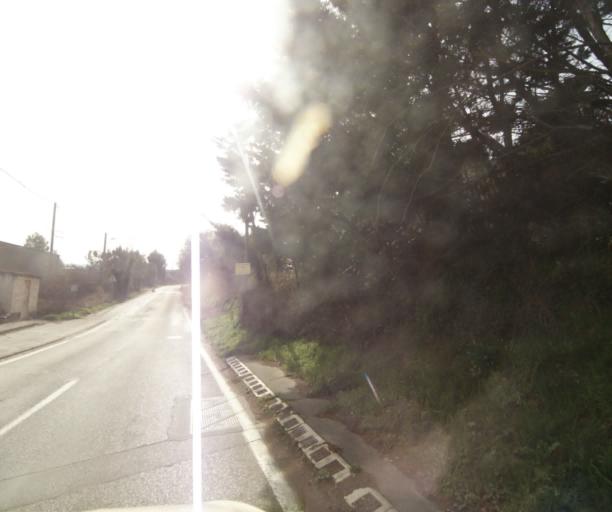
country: FR
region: Provence-Alpes-Cote d'Azur
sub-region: Departement des Bouches-du-Rhone
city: Gardanne
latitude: 43.4676
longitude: 5.4795
